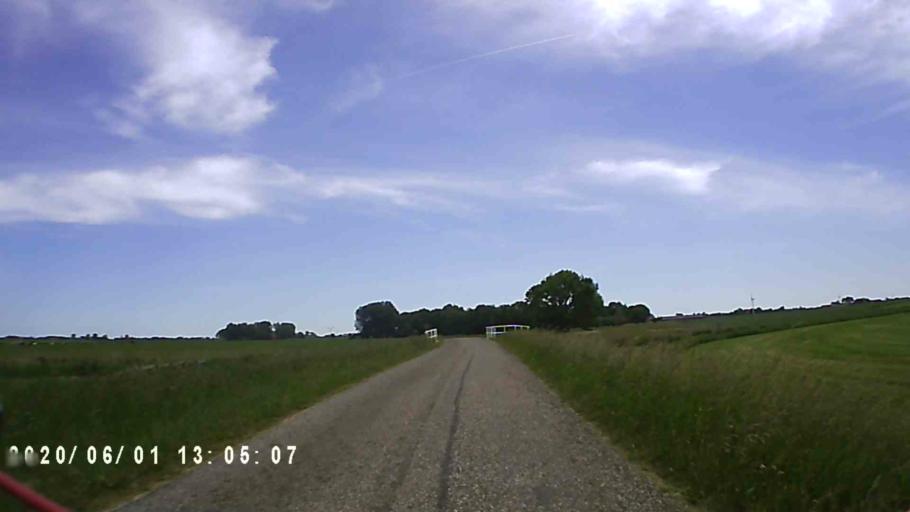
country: NL
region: Friesland
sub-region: Gemeente Franekeradeel
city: Tzum
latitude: 53.1376
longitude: 5.5467
